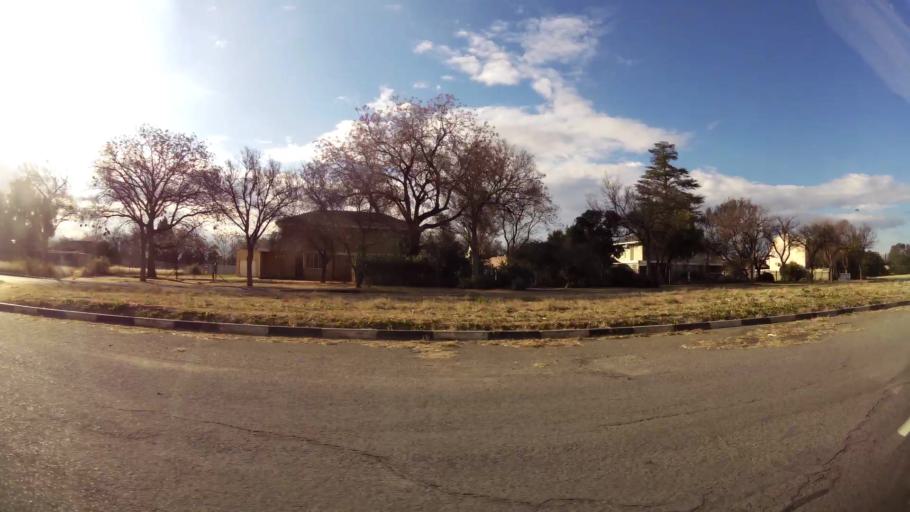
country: ZA
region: Orange Free State
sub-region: Lejweleputswa District Municipality
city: Welkom
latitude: -27.9872
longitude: 26.7103
